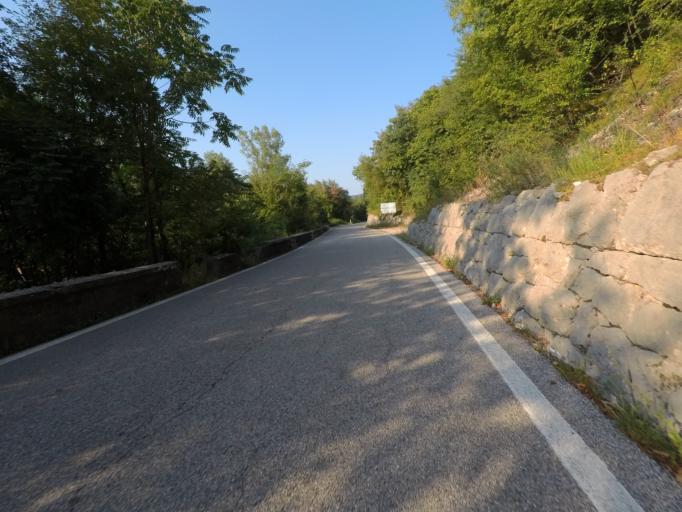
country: IT
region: Friuli Venezia Giulia
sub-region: Provincia di Udine
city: Forgaria nel Friuli
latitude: 46.2321
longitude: 13.0275
